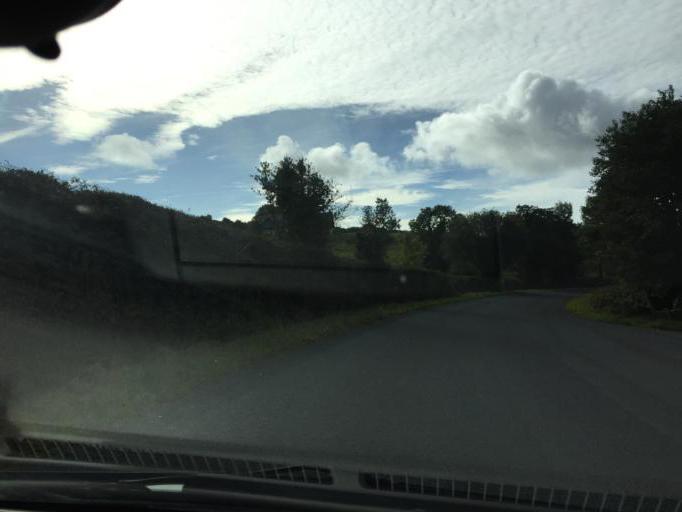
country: IE
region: Connaught
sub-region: Roscommon
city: Boyle
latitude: 54.0292
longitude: -8.3250
